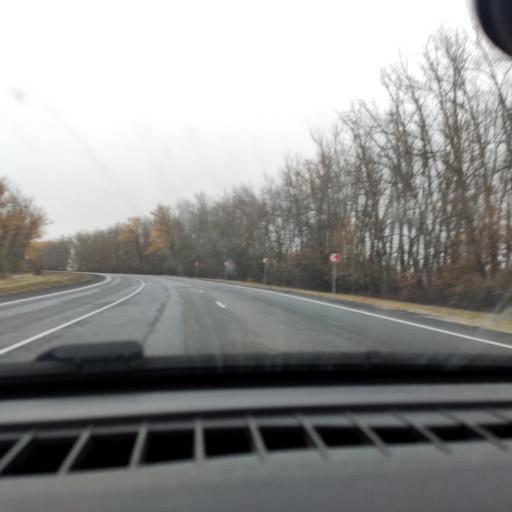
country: RU
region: Voronezj
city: Ostrogozhsk
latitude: 50.9470
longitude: 39.0538
